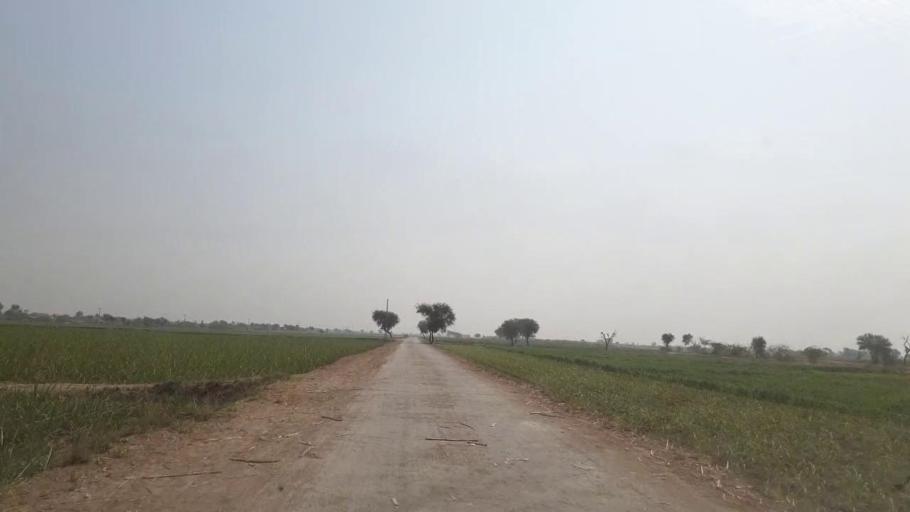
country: PK
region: Sindh
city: Mirpur Khas
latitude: 25.5413
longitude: 69.0859
